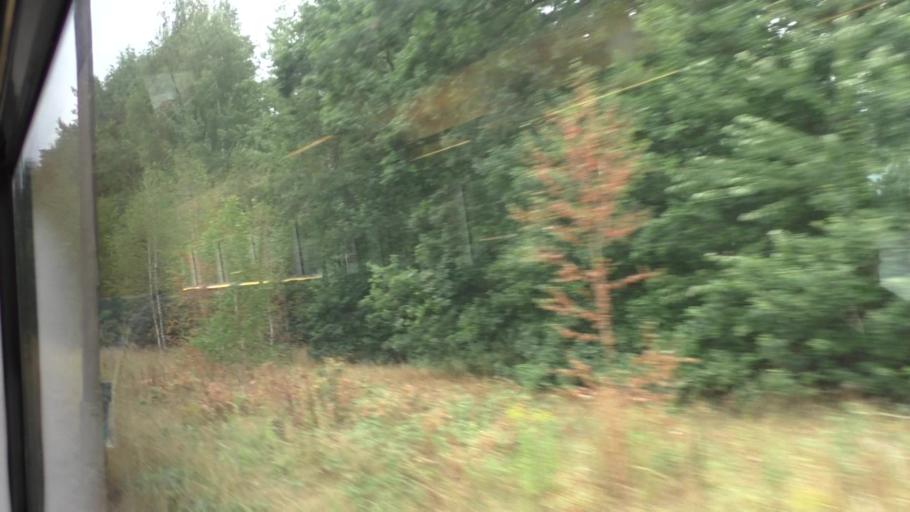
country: DE
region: Saxony
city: Goerlitz
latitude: 51.1298
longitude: 14.9718
